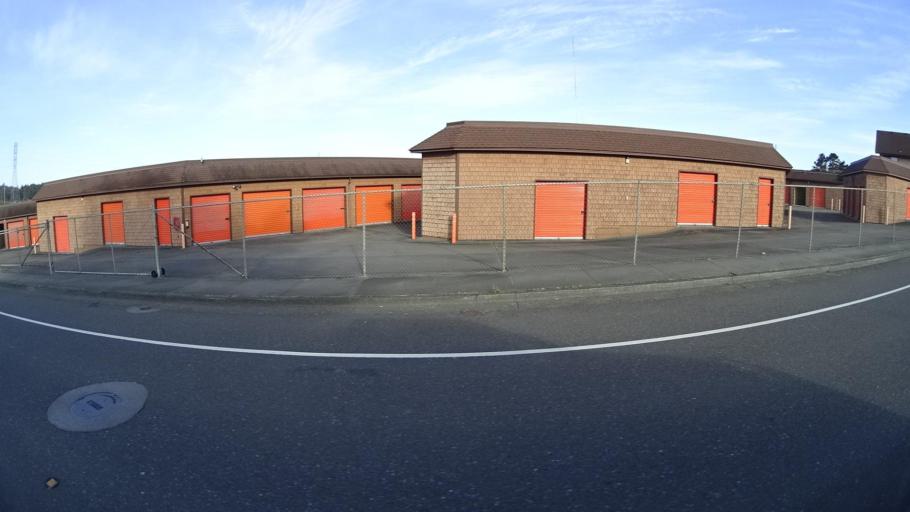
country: US
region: California
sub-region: Humboldt County
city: Humboldt Hill
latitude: 40.7400
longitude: -124.1994
